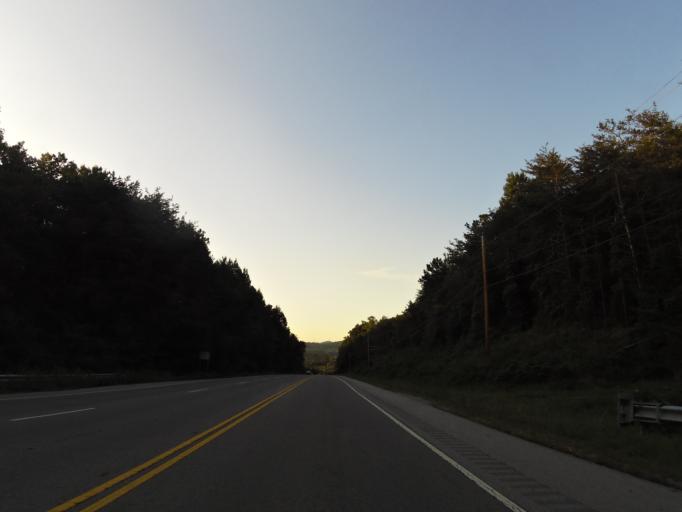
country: US
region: Tennessee
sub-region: Roane County
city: Midtown
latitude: 35.8424
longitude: -84.5425
